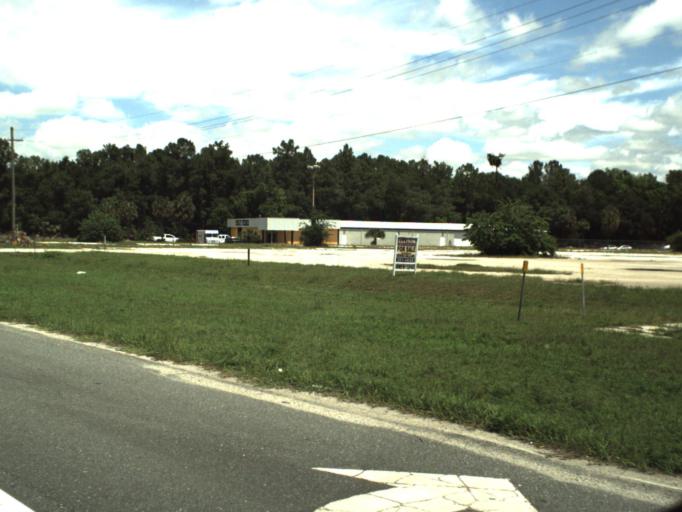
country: US
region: Florida
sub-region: Marion County
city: Ocala
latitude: 29.2164
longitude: -82.1453
